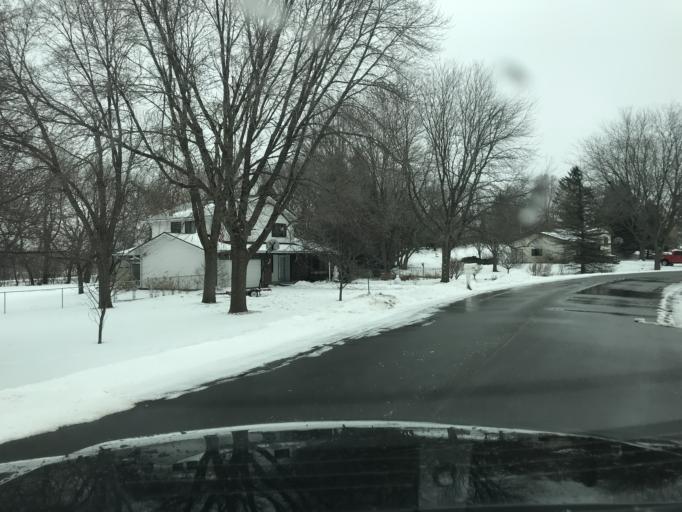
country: US
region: Wisconsin
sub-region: Dane County
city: Cottage Grove
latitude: 43.0879
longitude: -89.2205
